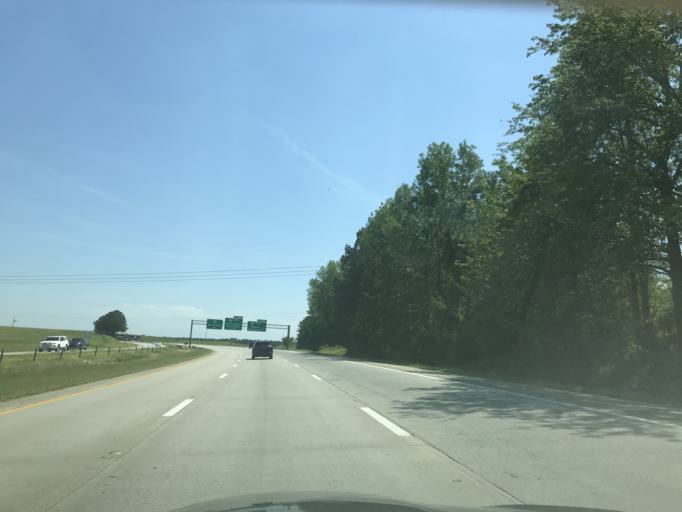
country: US
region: North Carolina
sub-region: Johnston County
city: Benson
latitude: 35.3960
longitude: -78.5224
